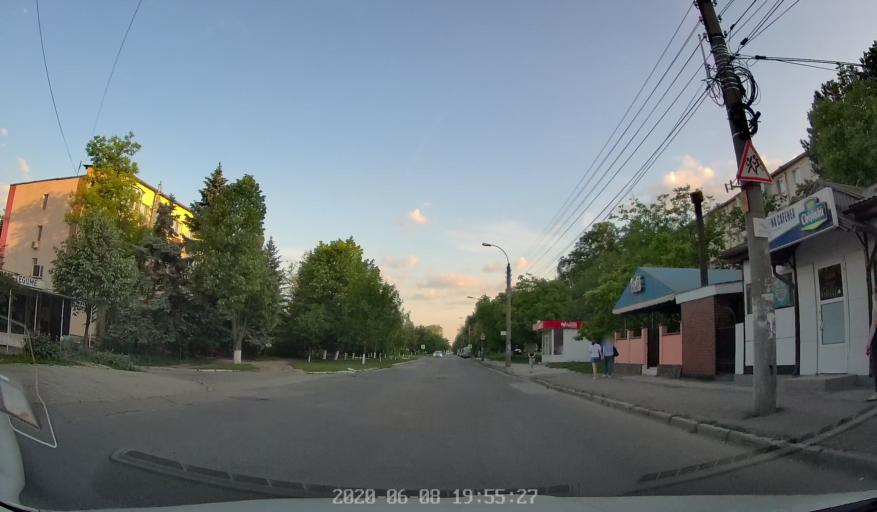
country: MD
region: Chisinau
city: Chisinau
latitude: 47.0288
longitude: 28.8838
